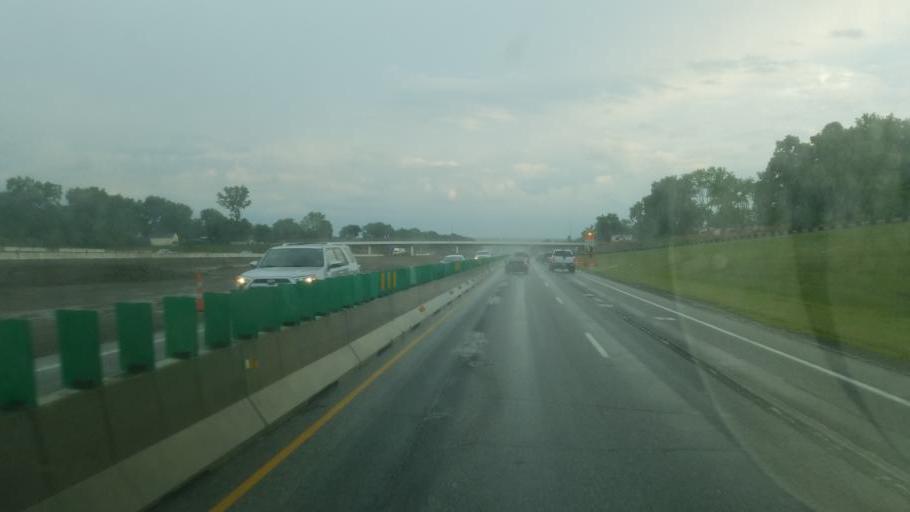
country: US
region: Ohio
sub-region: Cuyahoga County
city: Bedford Heights
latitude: 41.4054
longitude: -81.5069
